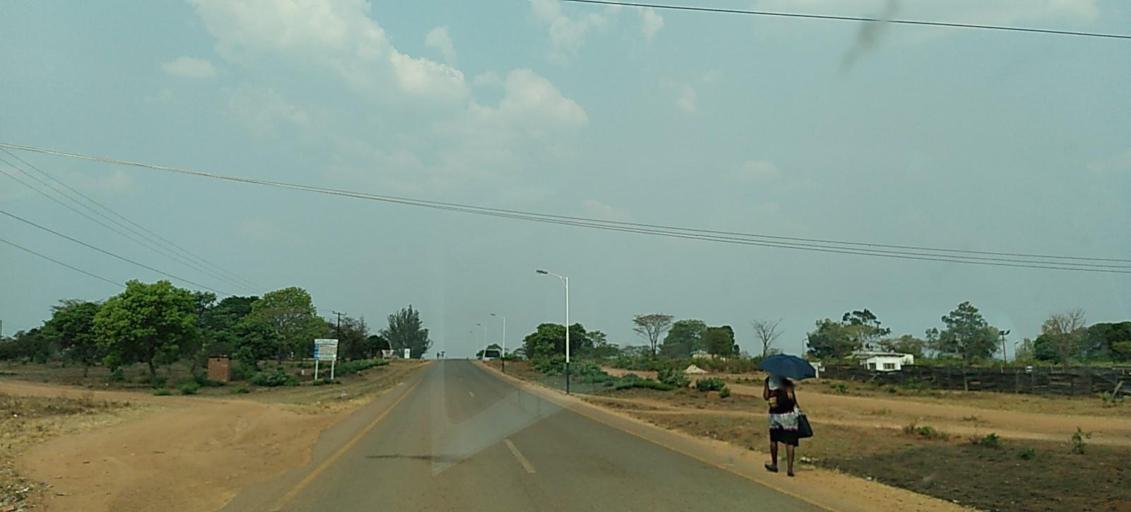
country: ZM
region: North-Western
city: Kabompo
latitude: -13.5928
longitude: 24.2056
